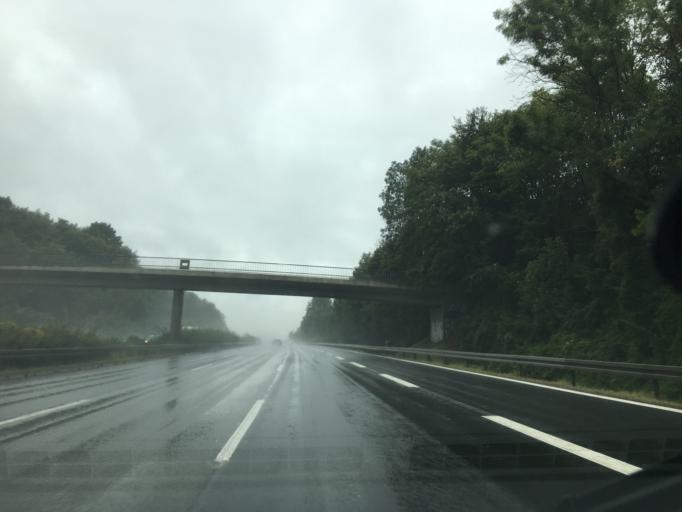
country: DE
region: North Rhine-Westphalia
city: Oelde
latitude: 51.8259
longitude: 8.1971
